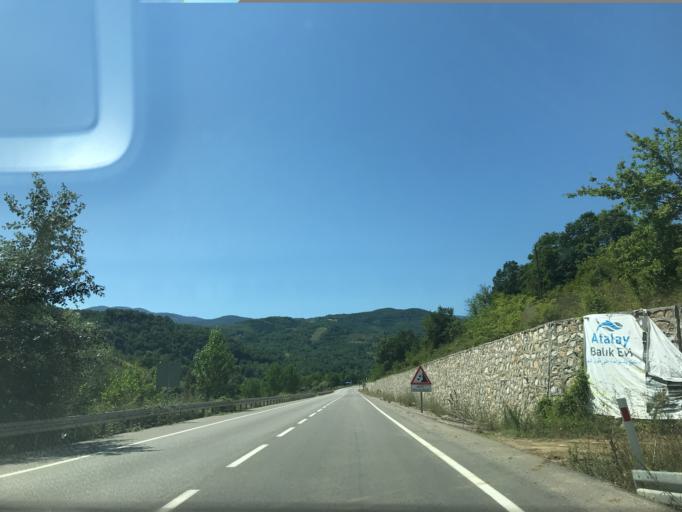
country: TR
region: Bursa
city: Tahtakopru
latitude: 39.9664
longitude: 29.6045
